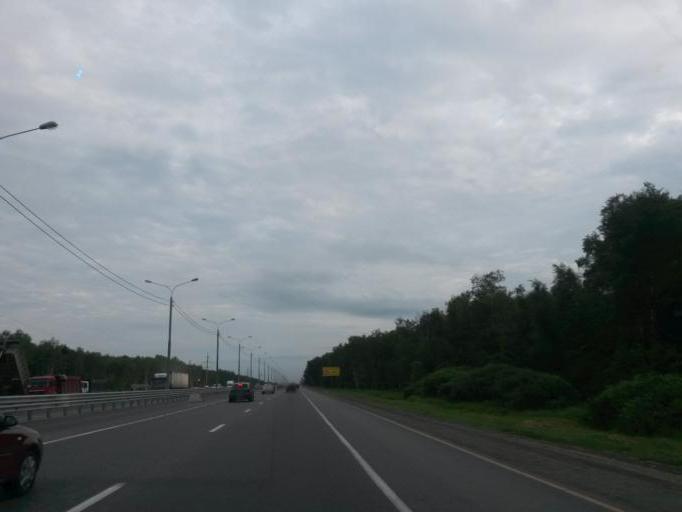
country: RU
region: Moskovskaya
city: L'vovskiy
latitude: 55.2924
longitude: 37.5441
